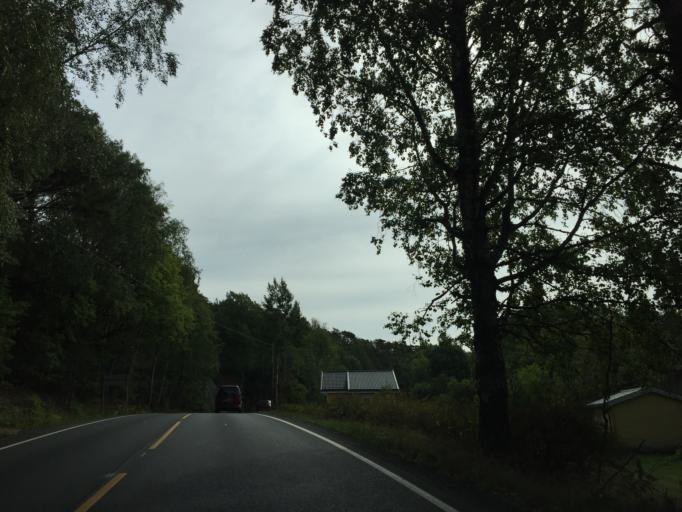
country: NO
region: Ostfold
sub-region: Fredrikstad
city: Fredrikstad
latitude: 59.1025
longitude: 10.9043
